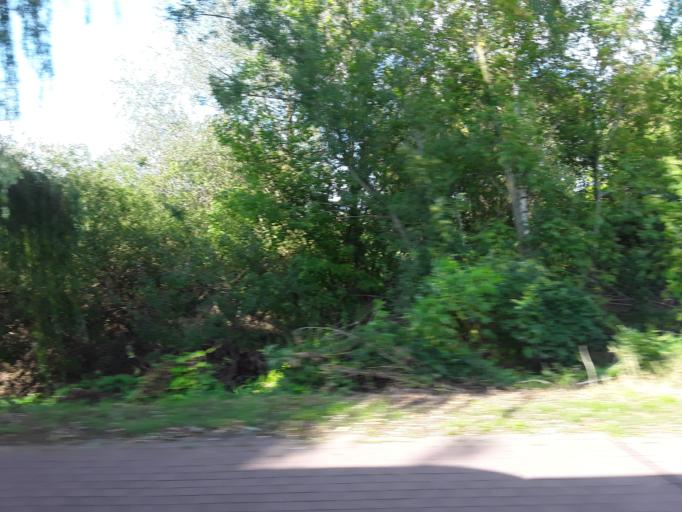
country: DE
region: Berlin
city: Buch
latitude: 52.6302
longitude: 13.5238
